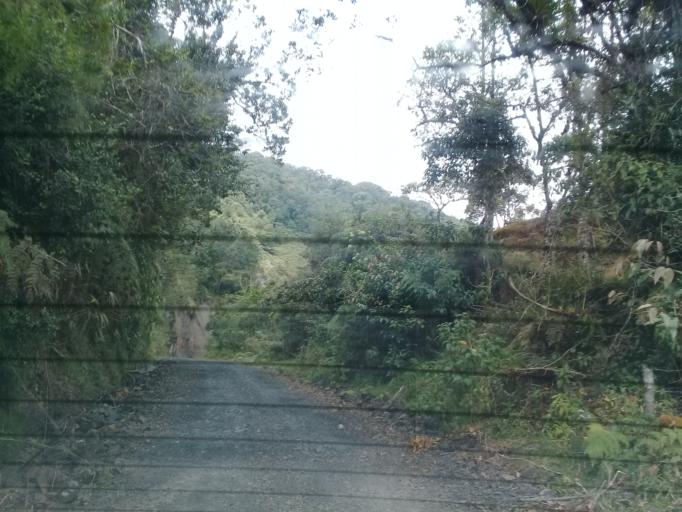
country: CO
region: Cundinamarca
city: Gachala
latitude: 4.7040
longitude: -73.4363
